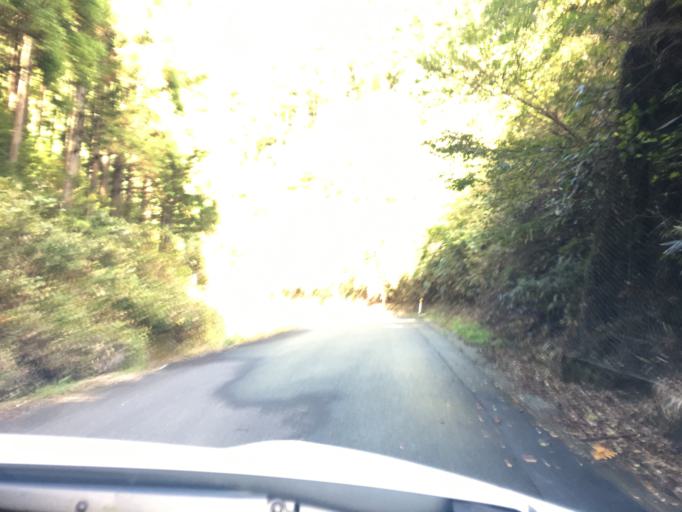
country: JP
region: Fukushima
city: Ishikawa
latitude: 37.1277
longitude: 140.5543
